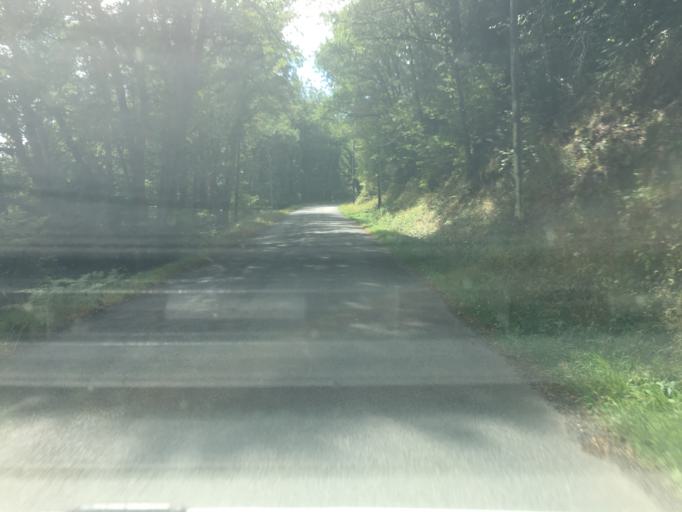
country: FR
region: Limousin
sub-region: Departement de la Correze
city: Neuvic
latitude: 45.4275
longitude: 2.3504
